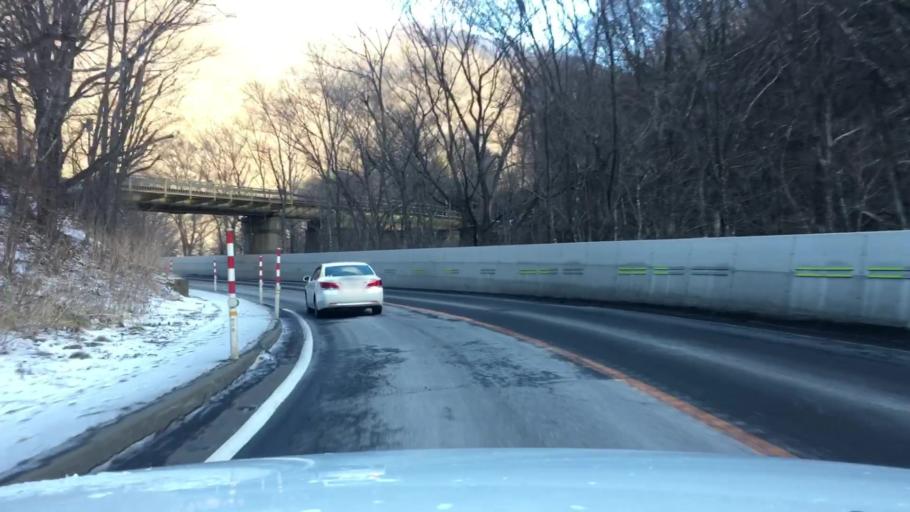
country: JP
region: Iwate
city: Tono
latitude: 39.6242
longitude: 141.5139
